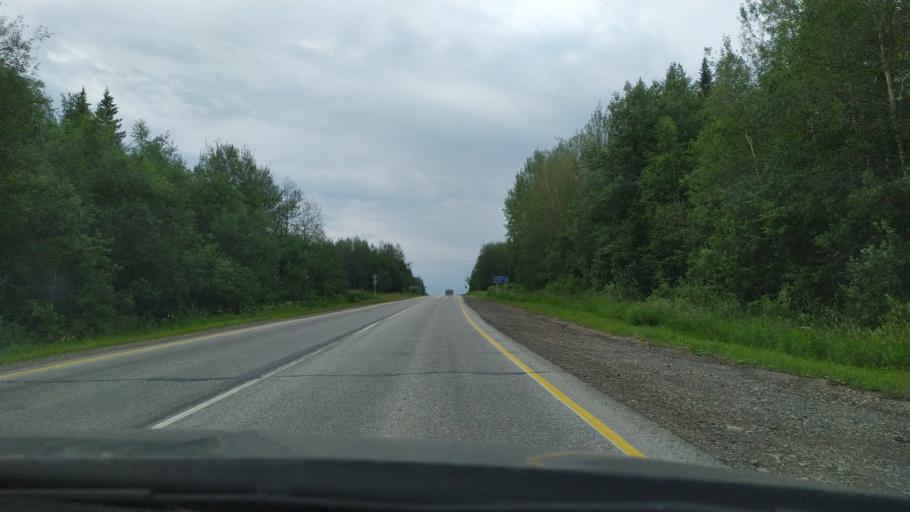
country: RU
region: Perm
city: Chusovoy
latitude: 58.3864
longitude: 57.9005
